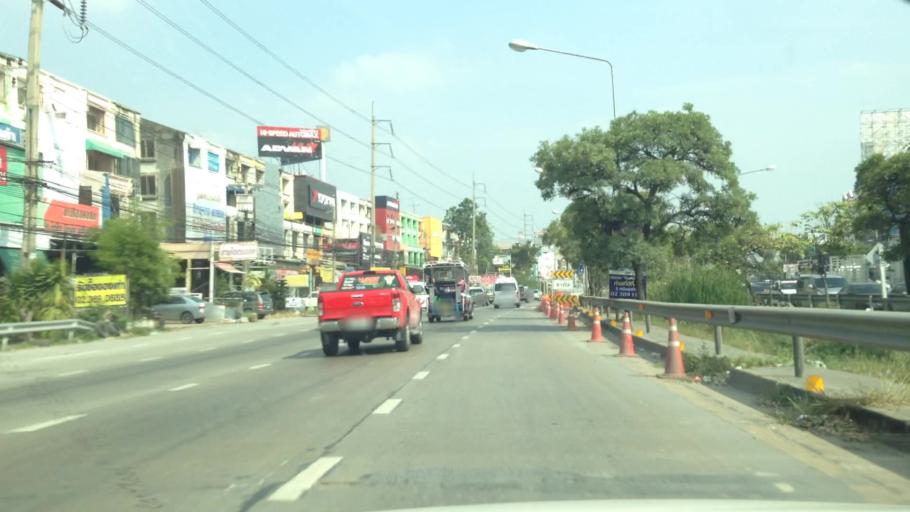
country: TH
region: Samut Prakan
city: Samut Prakan
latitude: 13.6010
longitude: 100.6128
